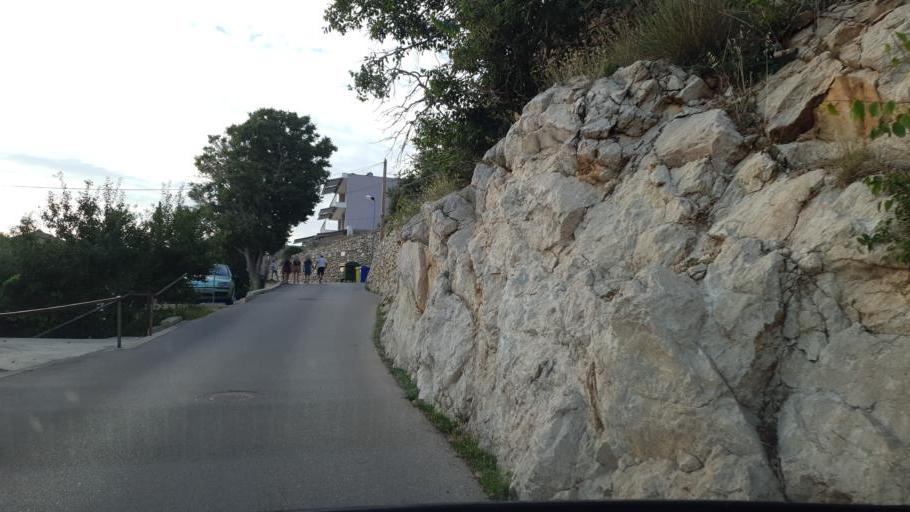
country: HR
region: Primorsko-Goranska
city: Punat
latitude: 44.9571
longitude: 14.6897
